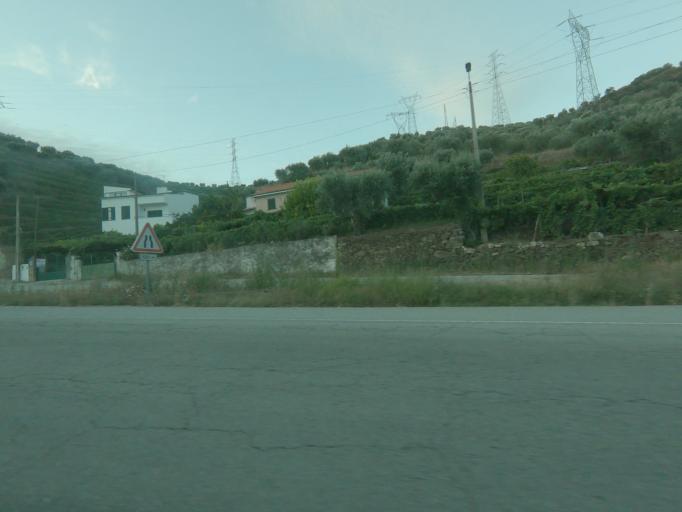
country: PT
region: Vila Real
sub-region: Peso da Regua
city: Peso da Regua
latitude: 41.1345
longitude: -7.7604
